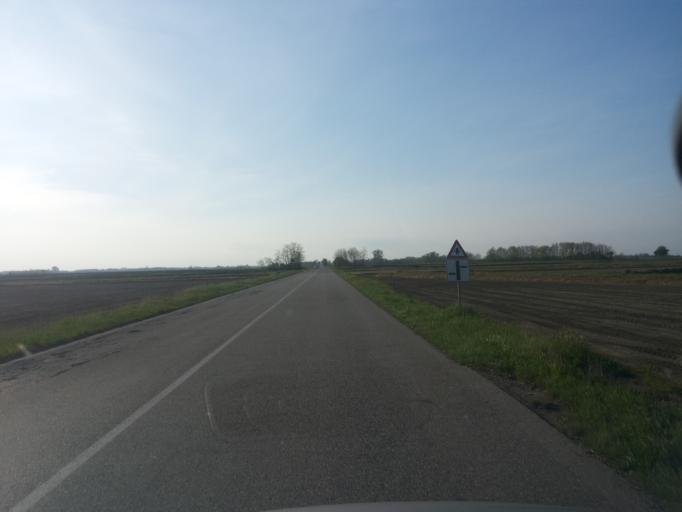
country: IT
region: Lombardy
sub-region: Provincia di Pavia
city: Candia Lomellina
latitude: 45.1942
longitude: 8.5918
